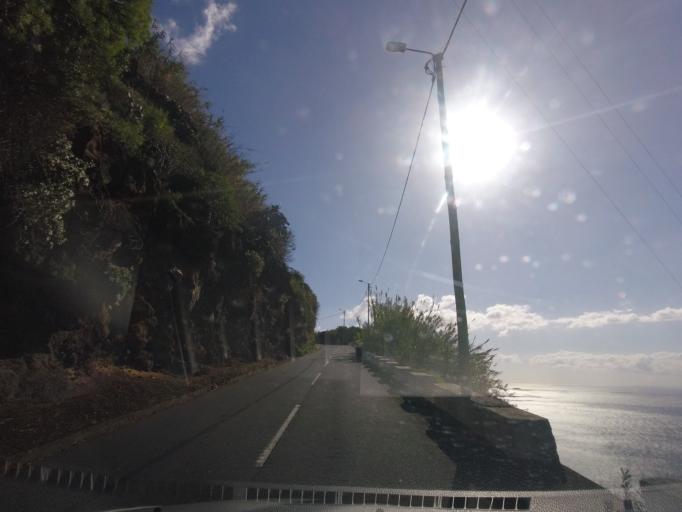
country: PT
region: Madeira
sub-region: Calheta
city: Estreito da Calheta
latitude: 32.7342
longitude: -17.1987
